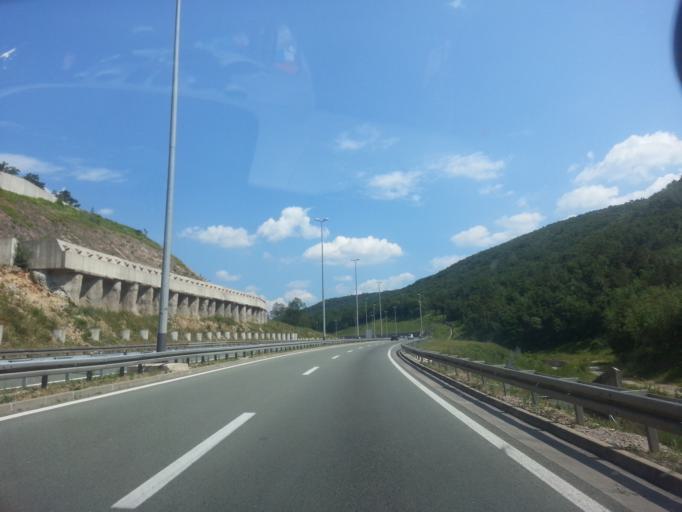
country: HR
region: Primorsko-Goranska
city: Skrljevo
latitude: 45.3188
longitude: 14.5010
